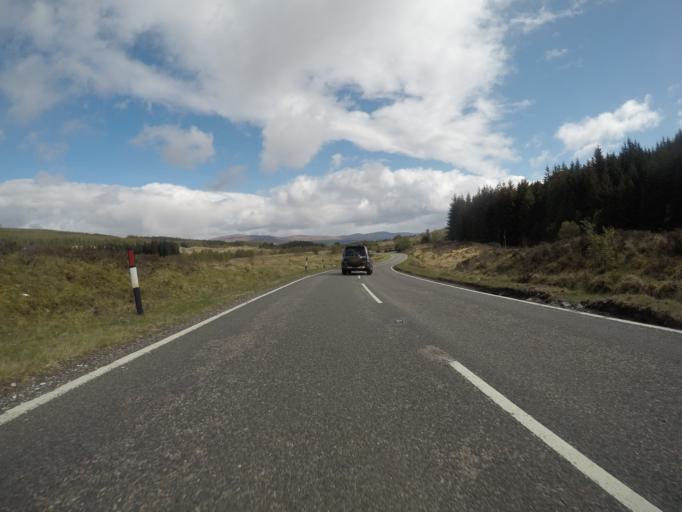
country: GB
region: Scotland
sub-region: Highland
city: Spean Bridge
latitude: 57.1276
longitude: -4.9645
